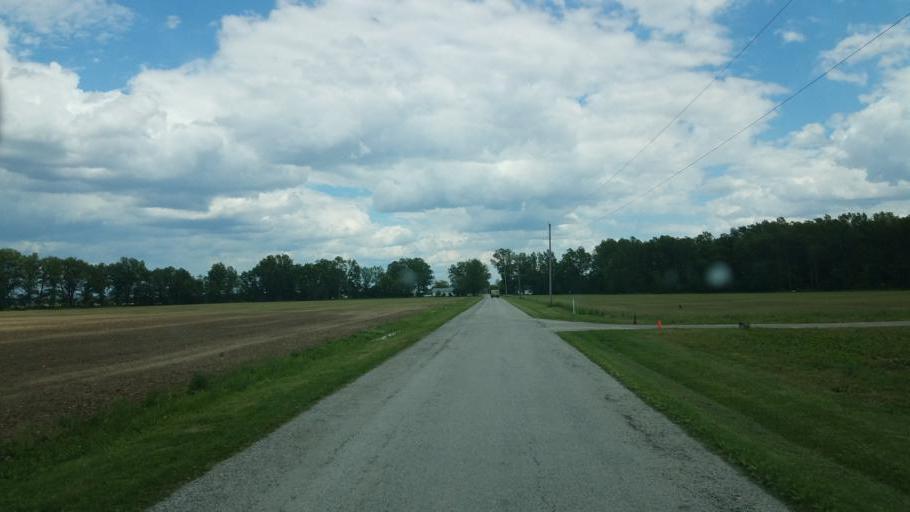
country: US
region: Ohio
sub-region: Huron County
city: Monroeville
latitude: 41.2196
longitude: -82.7261
